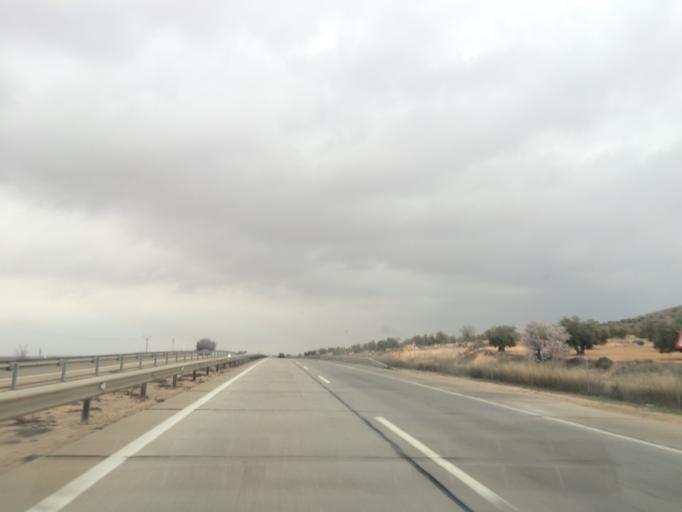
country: ES
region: Castille-La Mancha
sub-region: Province of Toledo
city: Madridejos
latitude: 39.5298
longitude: -3.5213
